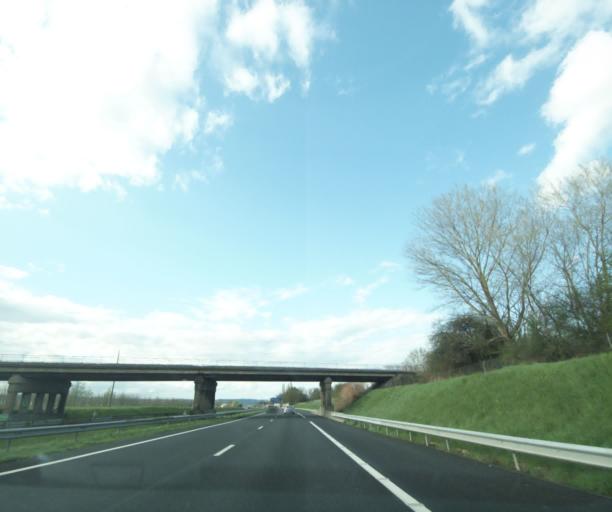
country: FR
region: Rhone-Alpes
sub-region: Departement du Rhone
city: Les Cheres
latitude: 45.8795
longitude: 4.7395
